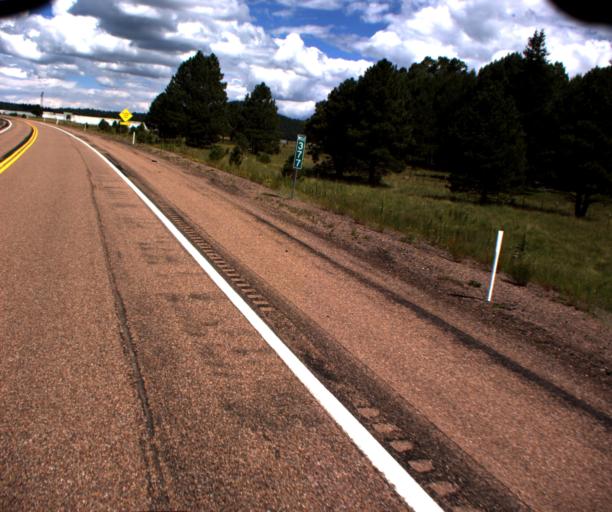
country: US
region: Arizona
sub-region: Apache County
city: Eagar
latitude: 34.0402
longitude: -109.5992
